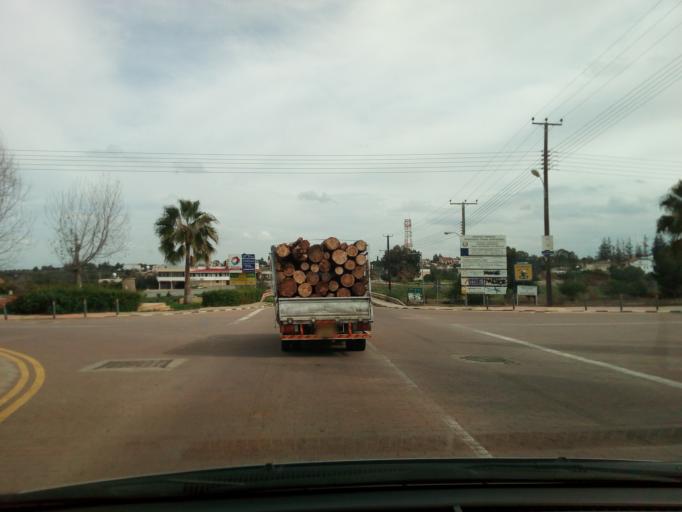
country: CY
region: Lefkosia
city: Peristerona
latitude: 35.1330
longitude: 33.0794
